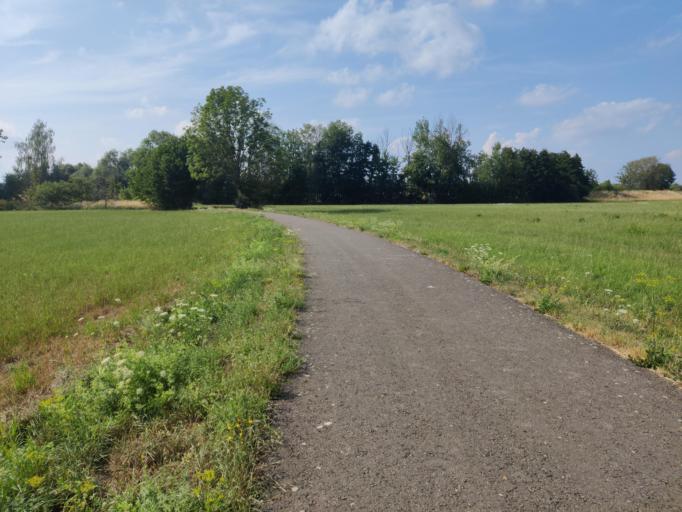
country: DE
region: Thuringia
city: Haselbach
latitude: 51.0656
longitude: 12.4444
